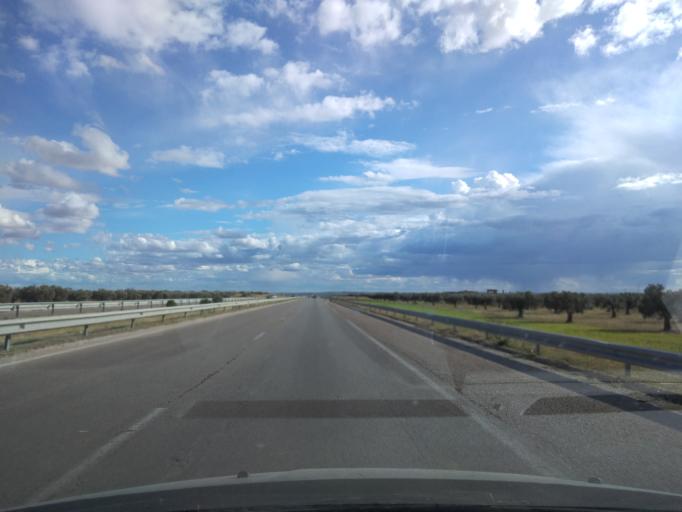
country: TN
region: Al Munastir
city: Manzil Kamil
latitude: 35.6169
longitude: 10.5954
